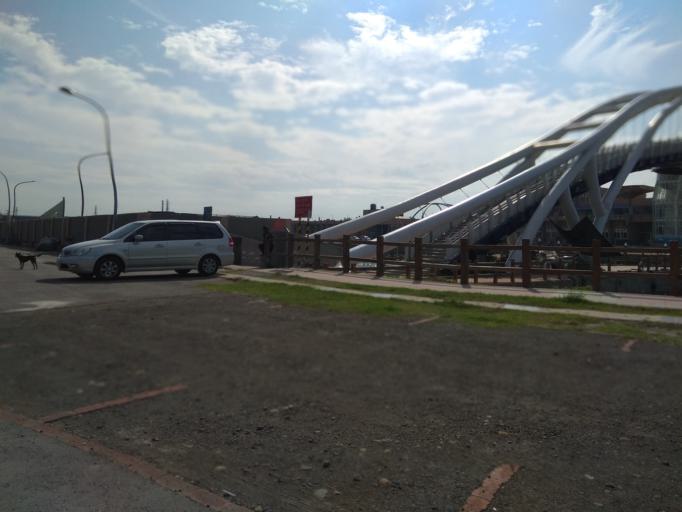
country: TW
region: Taiwan
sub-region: Hsinchu
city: Zhubei
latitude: 24.9894
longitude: 121.0148
